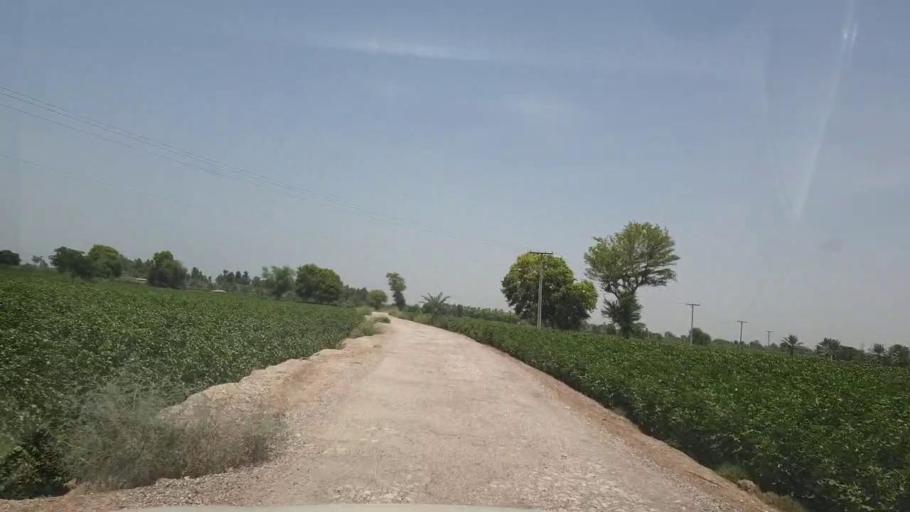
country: PK
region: Sindh
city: Bozdar
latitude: 27.1626
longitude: 68.6191
